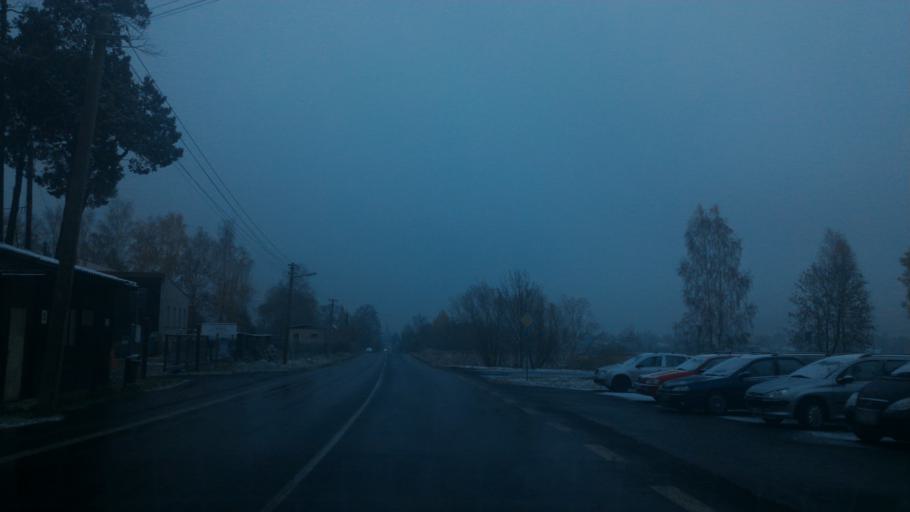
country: CZ
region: Ustecky
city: Jirikov
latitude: 50.9811
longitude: 14.5672
